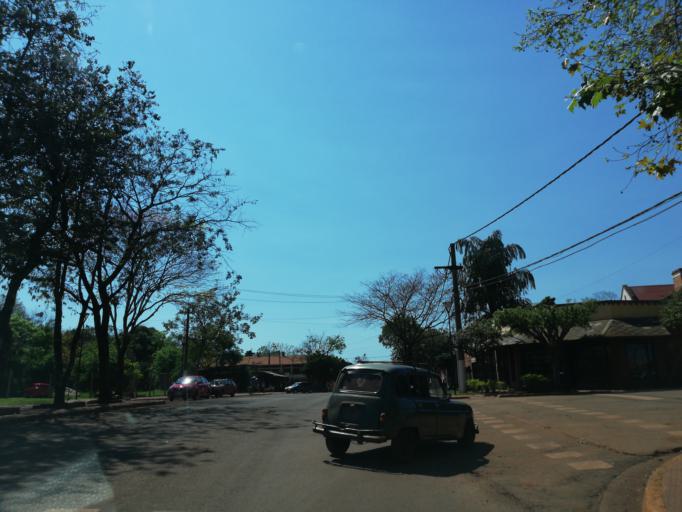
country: AR
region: Misiones
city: Puerto Eldorado
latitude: -26.4072
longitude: -54.6677
